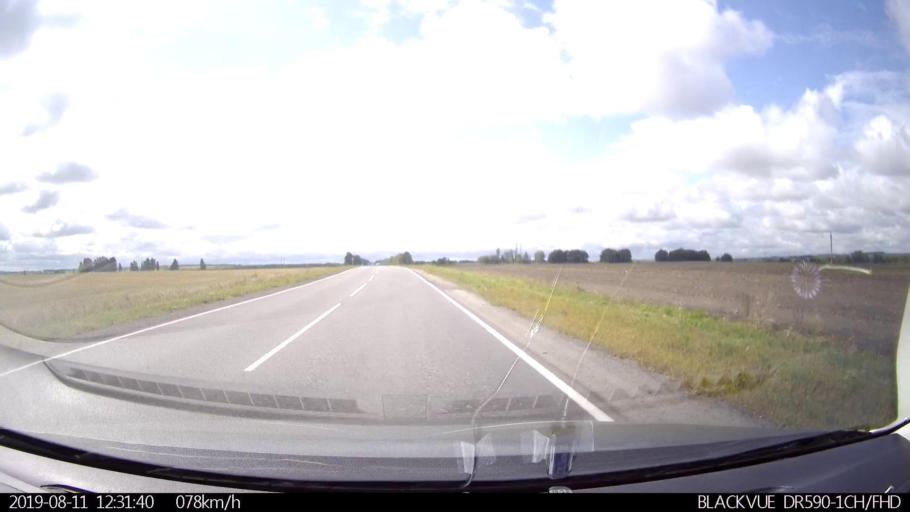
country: RU
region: Ulyanovsk
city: Ignatovka
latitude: 53.8182
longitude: 47.8810
